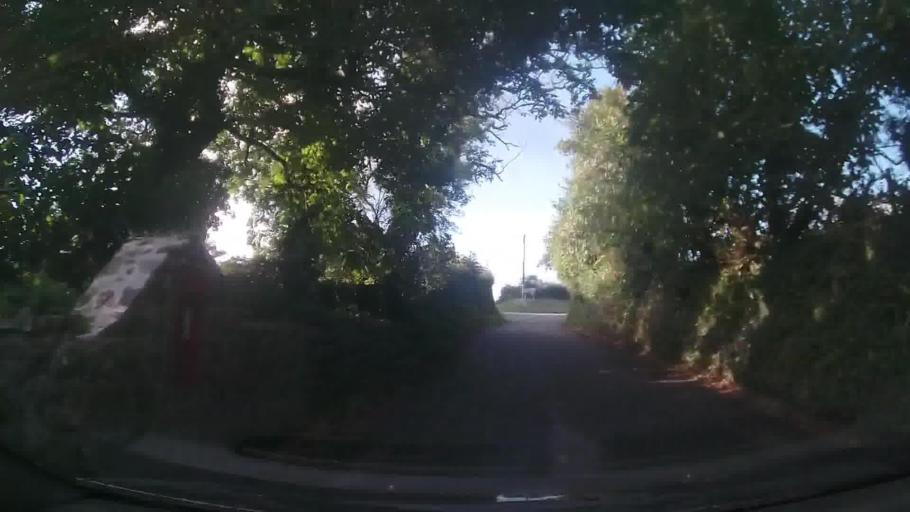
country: GB
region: Wales
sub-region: Pembrokeshire
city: Saundersfoot
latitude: 51.7402
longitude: -4.6618
